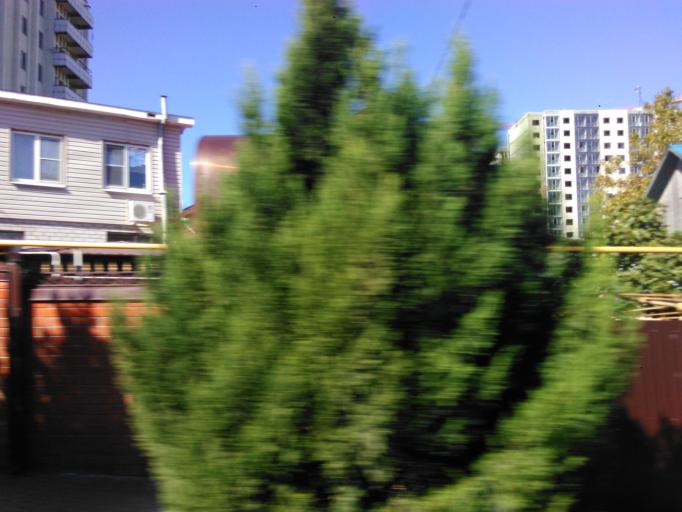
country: RU
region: Krasnodarskiy
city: Gelendzhik
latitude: 44.5520
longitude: 38.0628
